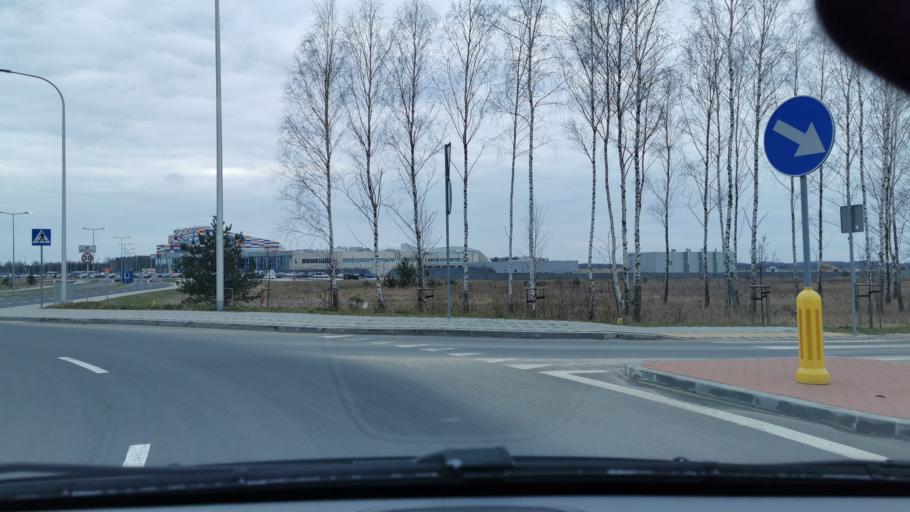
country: PL
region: Masovian Voivodeship
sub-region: Powiat zyrardowski
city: Mszczonow
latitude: 51.9910
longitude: 20.4636
